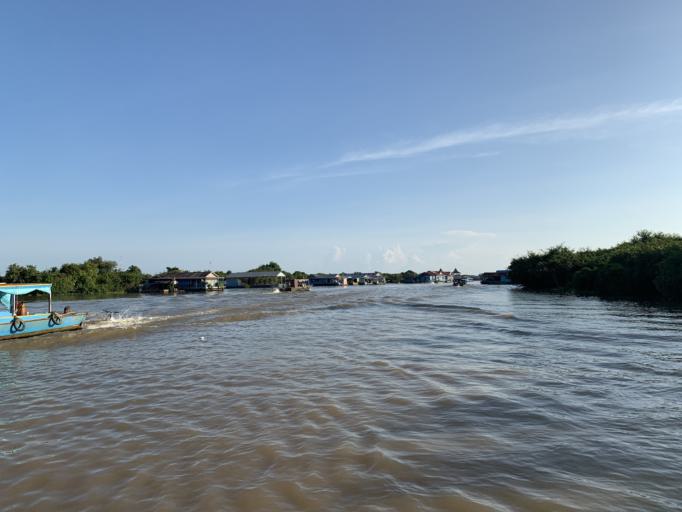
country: KH
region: Siem Reap
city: Siem Reap
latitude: 13.2469
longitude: 103.8232
